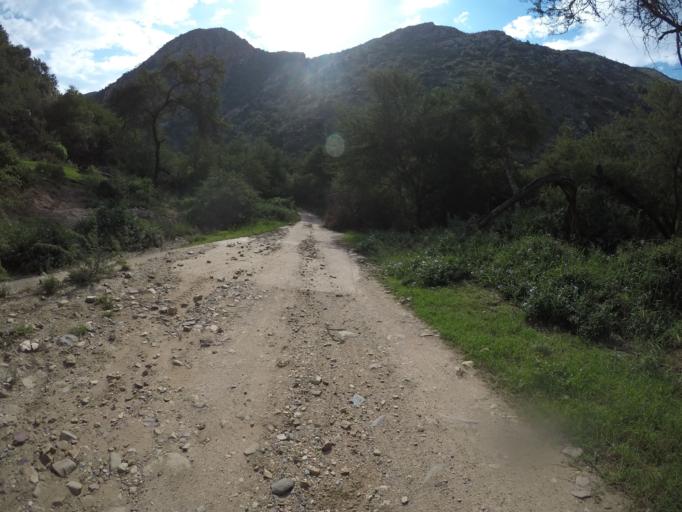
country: ZA
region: Eastern Cape
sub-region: Cacadu District Municipality
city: Kareedouw
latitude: -33.6367
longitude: 24.3215
